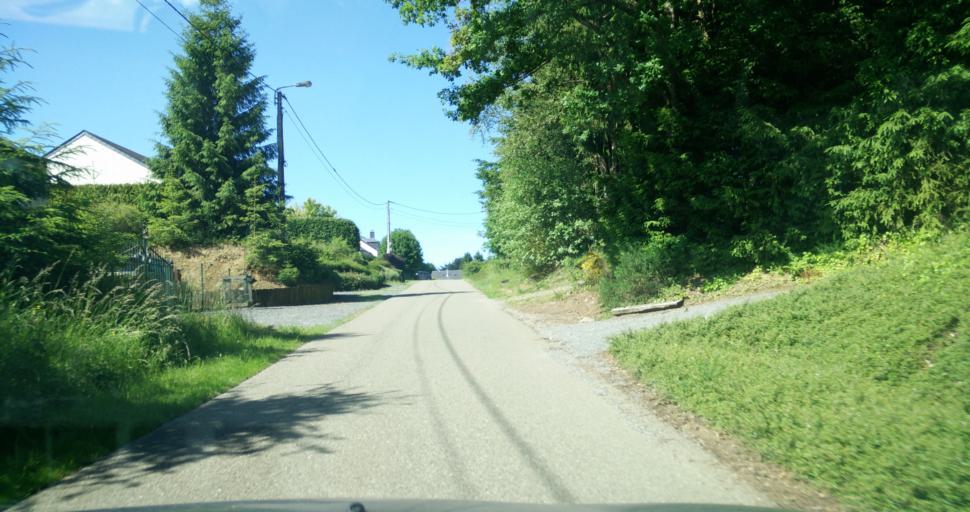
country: BE
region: Wallonia
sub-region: Province du Luxembourg
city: Houffalize
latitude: 50.1660
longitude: 5.7296
